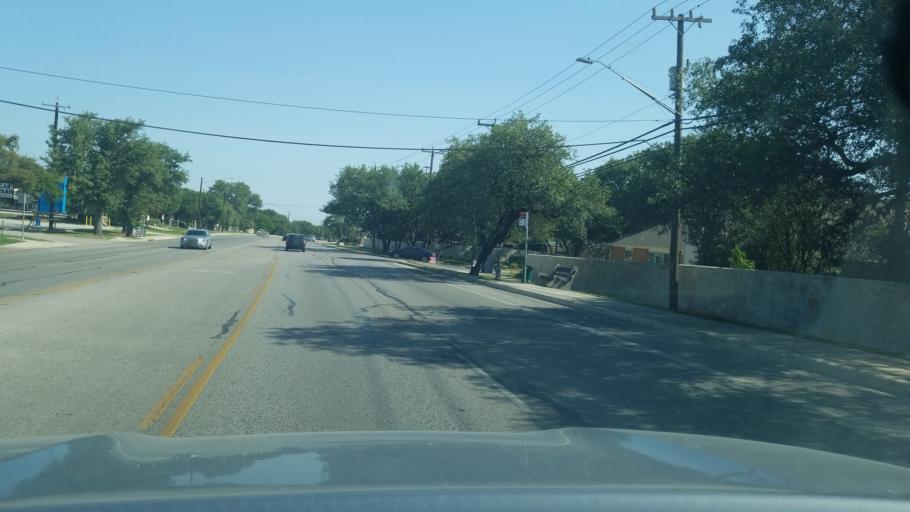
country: US
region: Texas
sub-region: Bexar County
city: Hollywood Park
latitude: 29.6045
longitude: -98.5084
